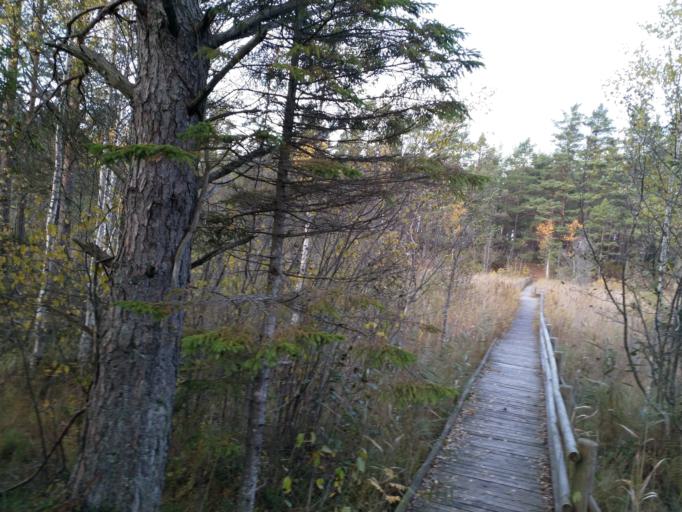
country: LV
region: Dundaga
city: Dundaga
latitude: 57.6487
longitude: 22.2573
